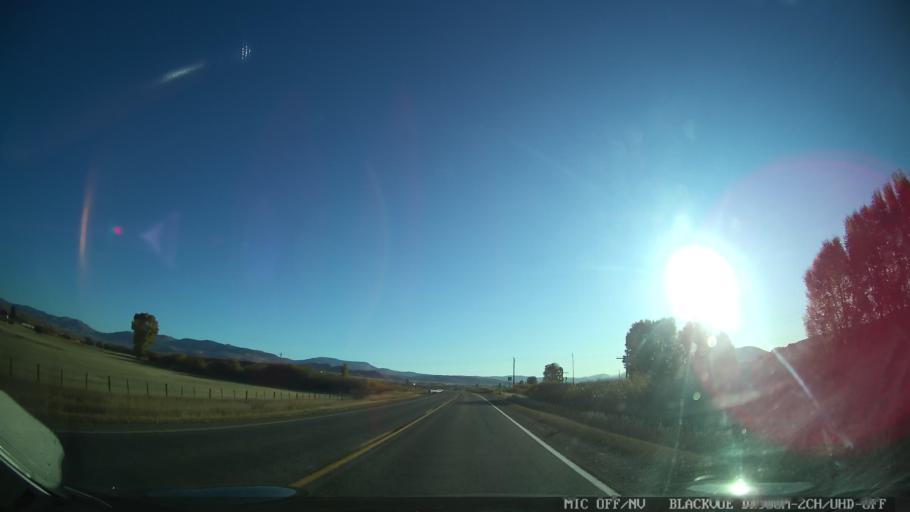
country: US
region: Colorado
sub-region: Grand County
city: Kremmling
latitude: 40.0582
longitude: -106.3077
